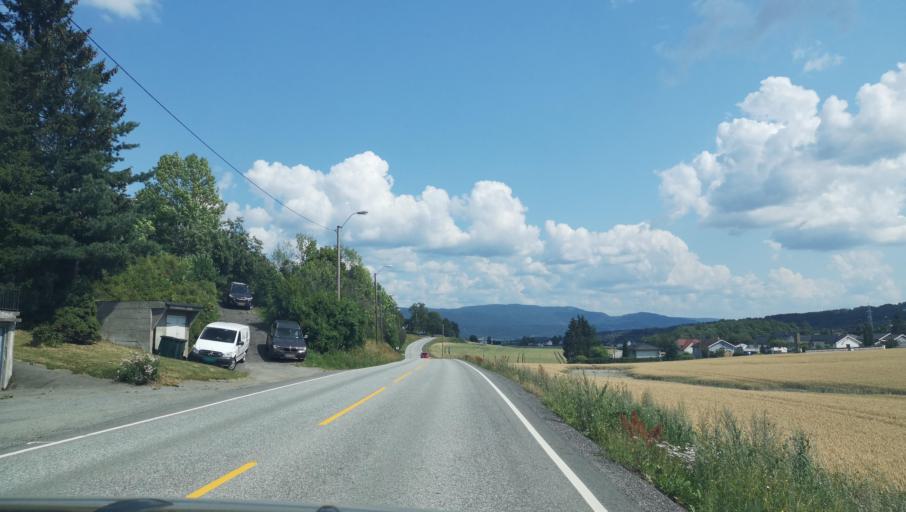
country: NO
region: Buskerud
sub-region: Ovre Eiker
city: Hokksund
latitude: 59.7370
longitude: 9.8545
